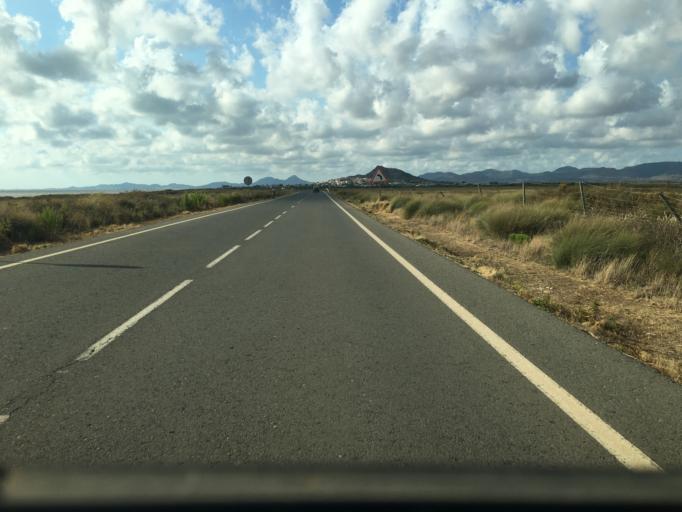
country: ES
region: Murcia
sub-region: Murcia
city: Los Alcazares
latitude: 37.7113
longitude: -0.8562
